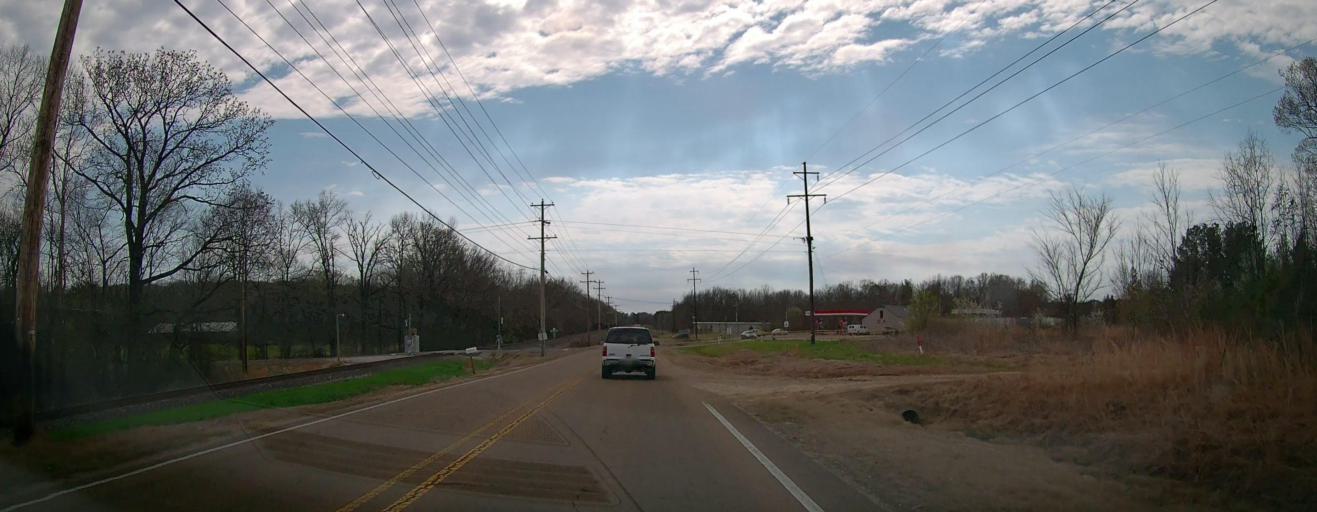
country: US
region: Mississippi
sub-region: Marshall County
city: Byhalia
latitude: 34.9000
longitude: -89.7428
